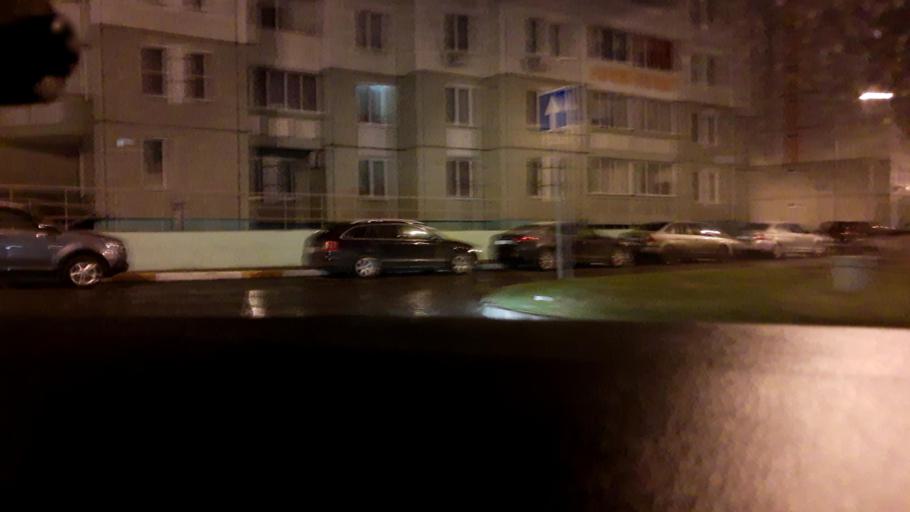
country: RU
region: Moskovskaya
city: Zheleznodorozhnyy
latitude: 55.7446
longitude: 37.9958
